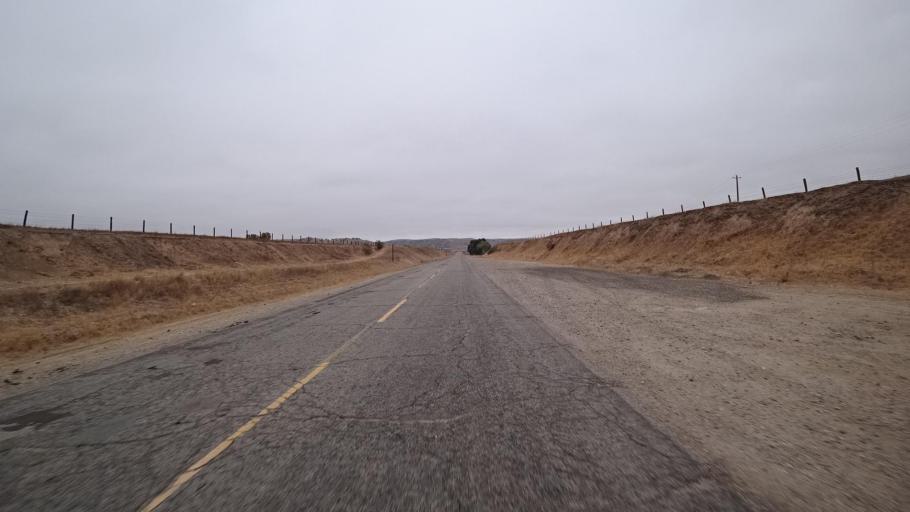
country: US
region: California
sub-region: San Luis Obispo County
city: San Miguel
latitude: 35.8625
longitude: -120.7933
